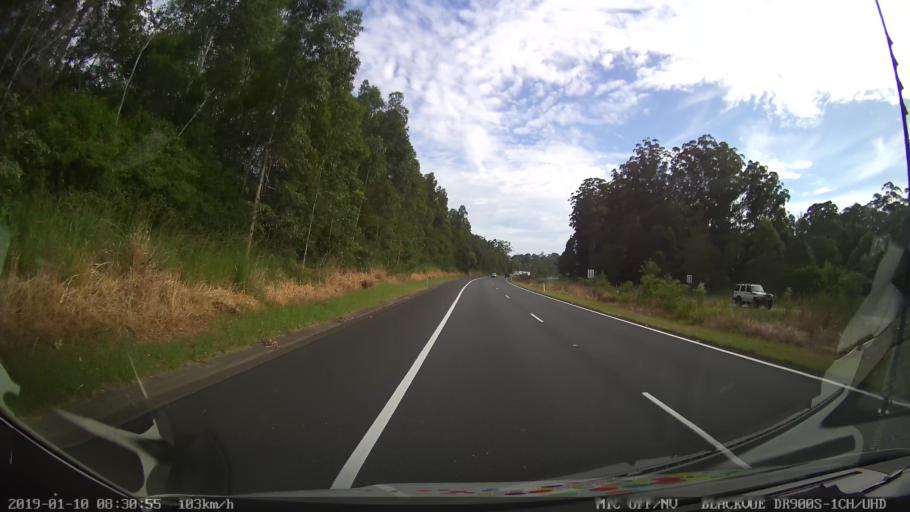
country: AU
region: New South Wales
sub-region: Coffs Harbour
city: Bonville
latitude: -30.3635
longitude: 153.0557
